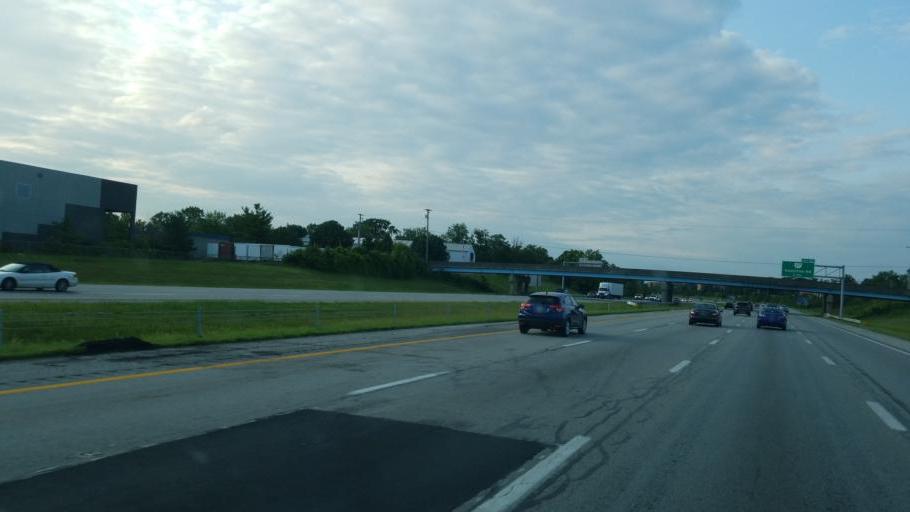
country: US
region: Ohio
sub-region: Franklin County
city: Gahanna
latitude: 39.9909
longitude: -82.8567
